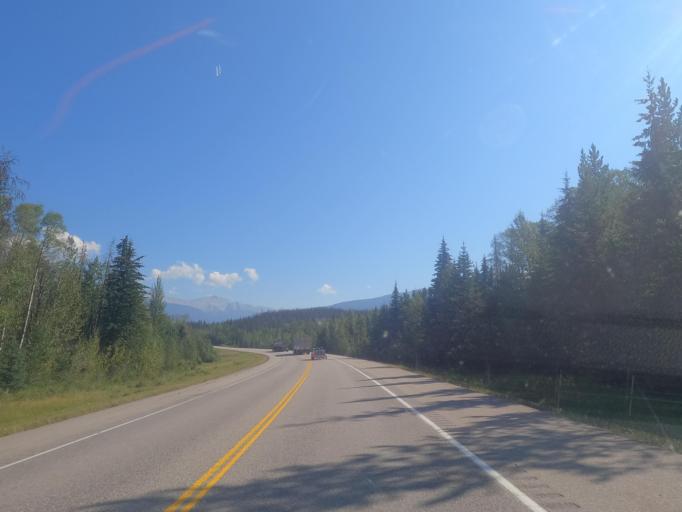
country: CA
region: Alberta
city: Jasper Park Lodge
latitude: 52.8577
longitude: -118.1186
